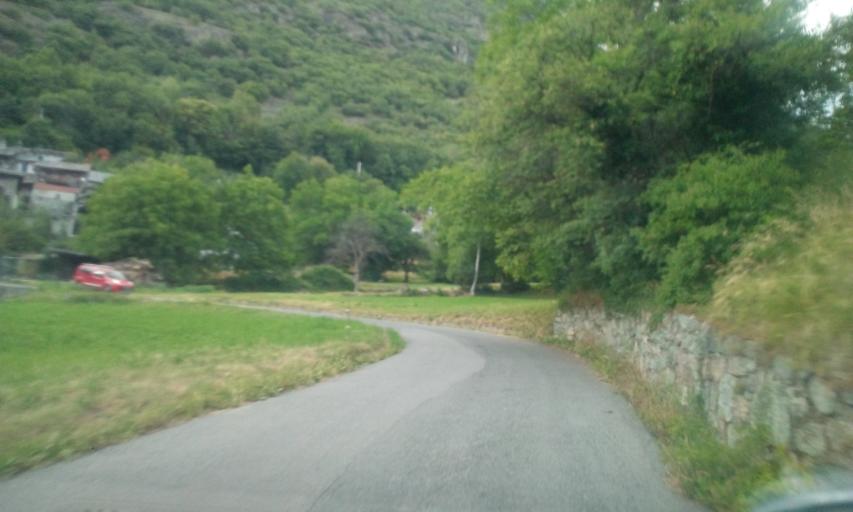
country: IT
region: Aosta Valley
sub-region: Valle d'Aosta
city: Saint-Vincent
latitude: 45.7572
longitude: 7.6352
